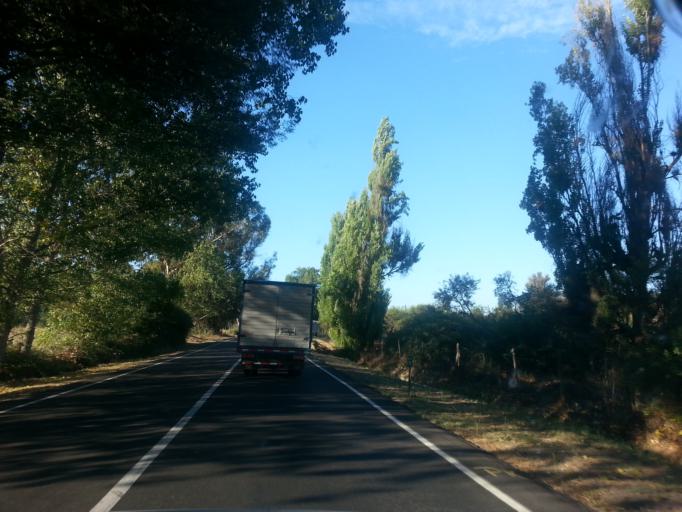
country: CL
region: Valparaiso
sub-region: Provincia de Marga Marga
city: Villa Alemana
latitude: -33.2086
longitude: -71.3858
